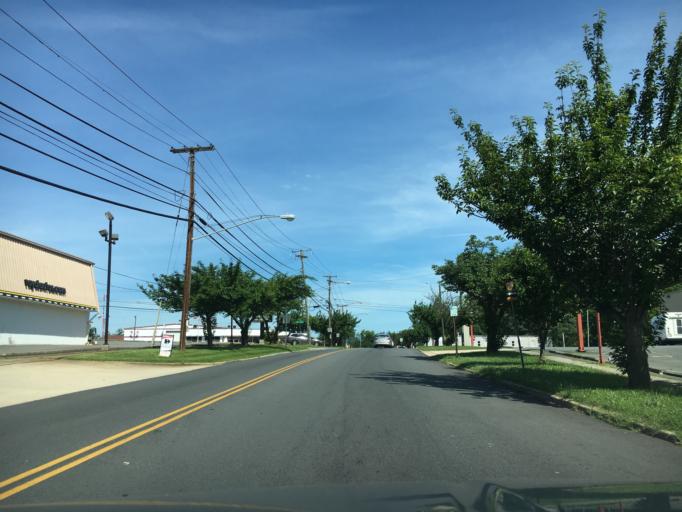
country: US
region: Virginia
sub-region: City of Lynchburg
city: West Lynchburg
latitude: 37.4001
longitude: -79.1732
